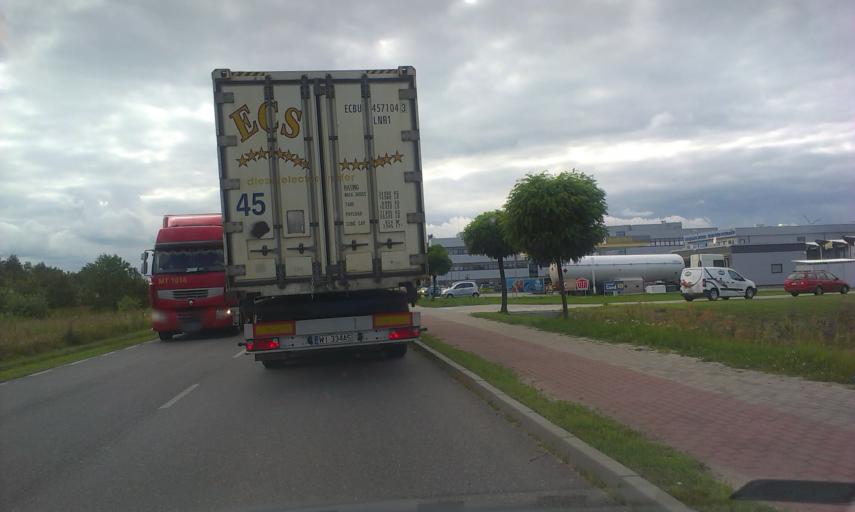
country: PL
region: Masovian Voivodeship
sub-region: Powiat zyrardowski
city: Mszczonow
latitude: 51.9733
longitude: 20.5439
